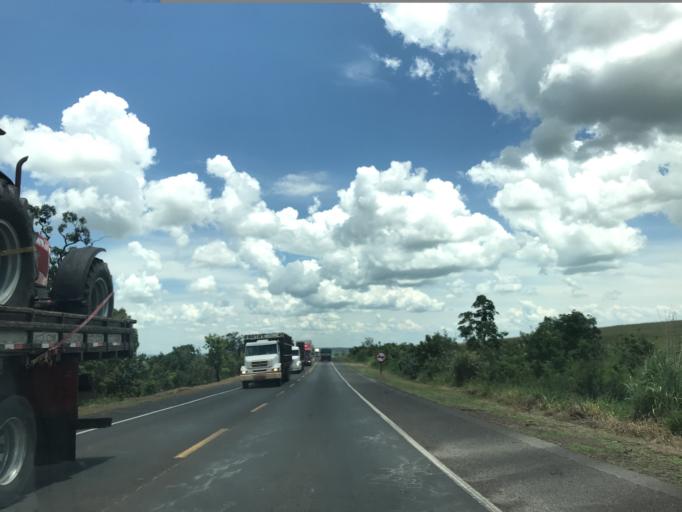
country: BR
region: Minas Gerais
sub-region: Prata
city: Prata
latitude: -19.5565
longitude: -48.8268
